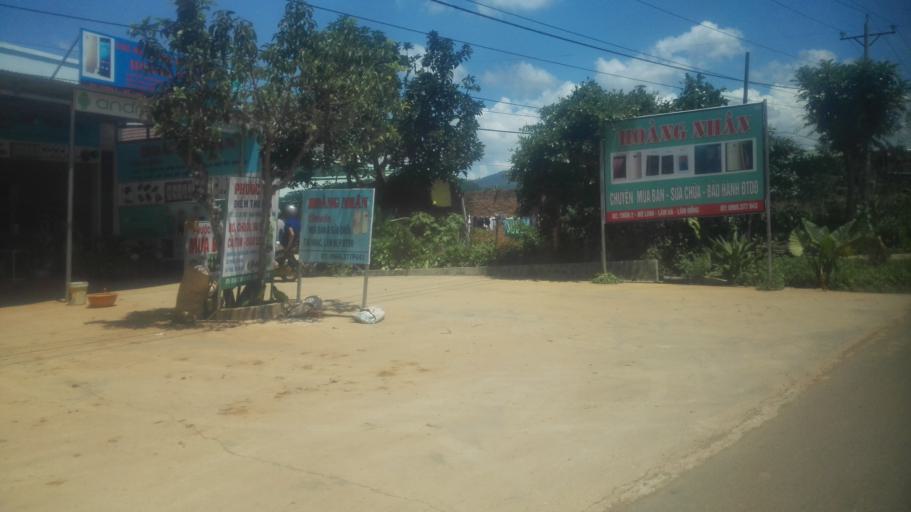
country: VN
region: Lam Dong
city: Da Lat
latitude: 11.8816
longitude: 108.3419
